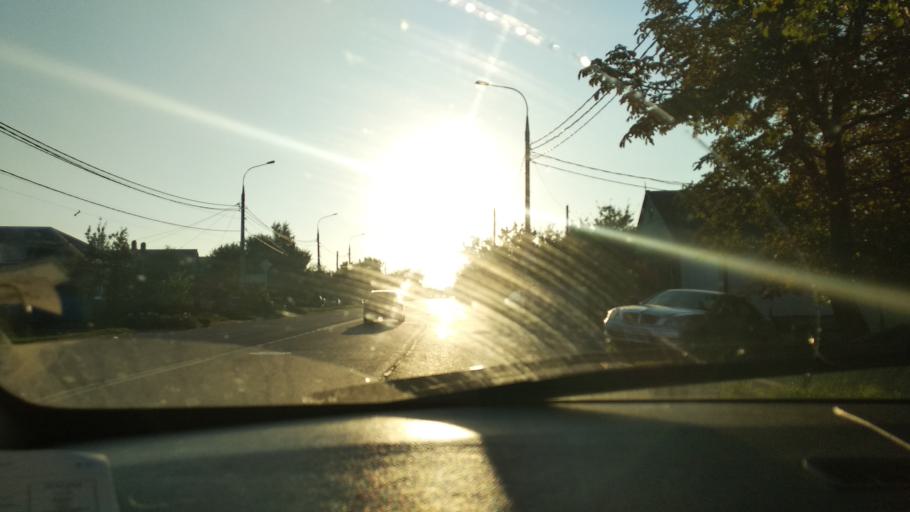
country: RU
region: Krasnodarskiy
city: Krasnodar
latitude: 45.0149
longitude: 39.0004
